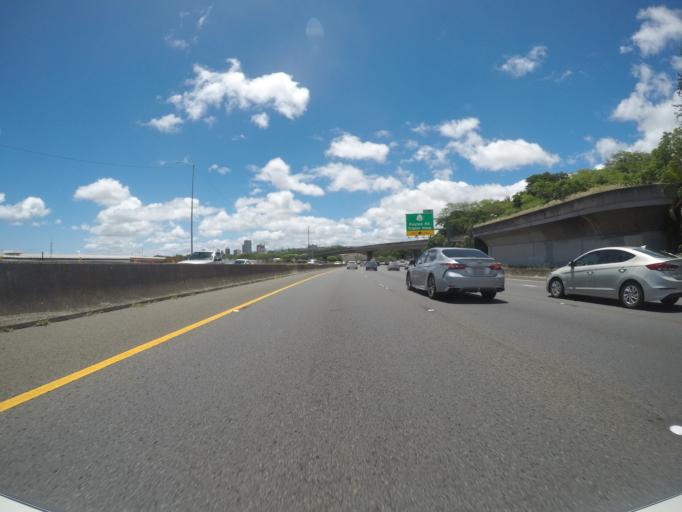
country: US
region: Hawaii
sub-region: Honolulu County
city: Halawa Heights
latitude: 21.3435
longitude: -157.8913
